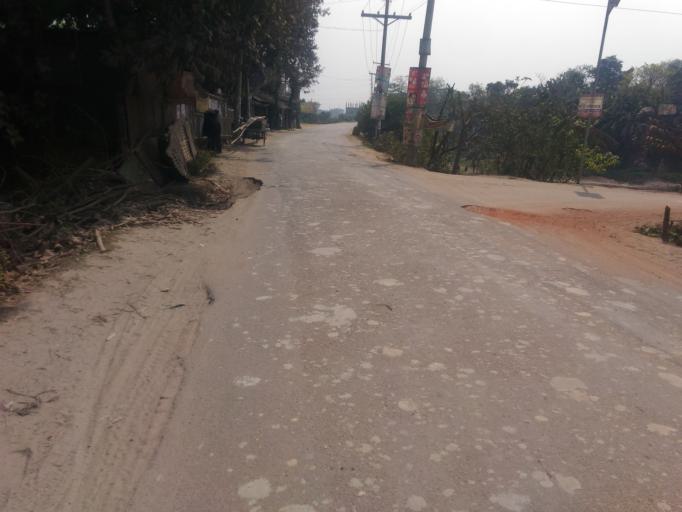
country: BD
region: Dhaka
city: Narayanganj
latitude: 23.6511
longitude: 90.4481
